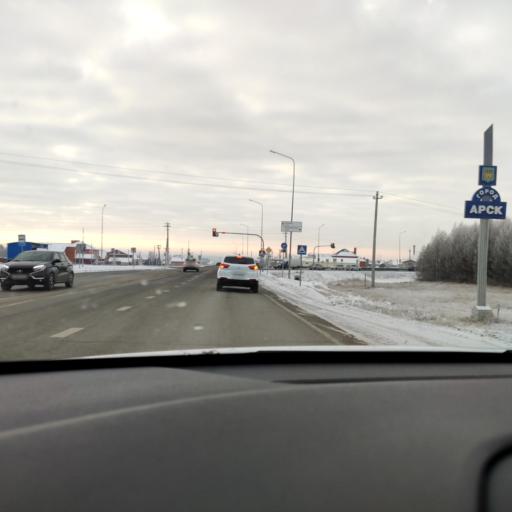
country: RU
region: Tatarstan
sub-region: Arskiy Rayon
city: Arsk
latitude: 56.1075
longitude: 49.8963
